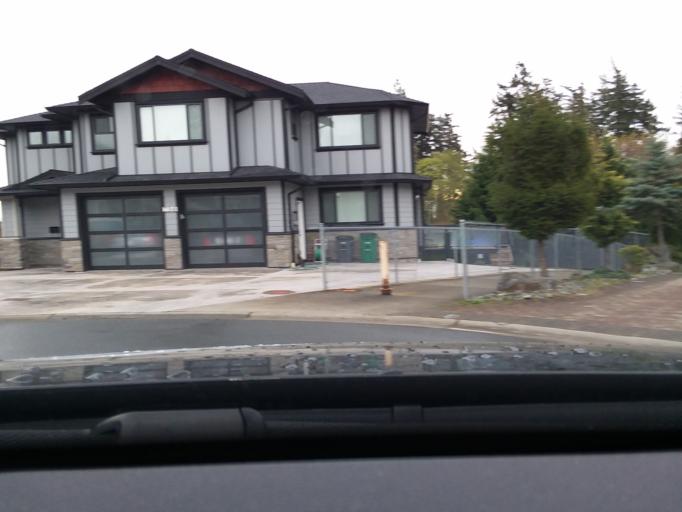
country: CA
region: British Columbia
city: Victoria
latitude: 48.5171
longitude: -123.3796
